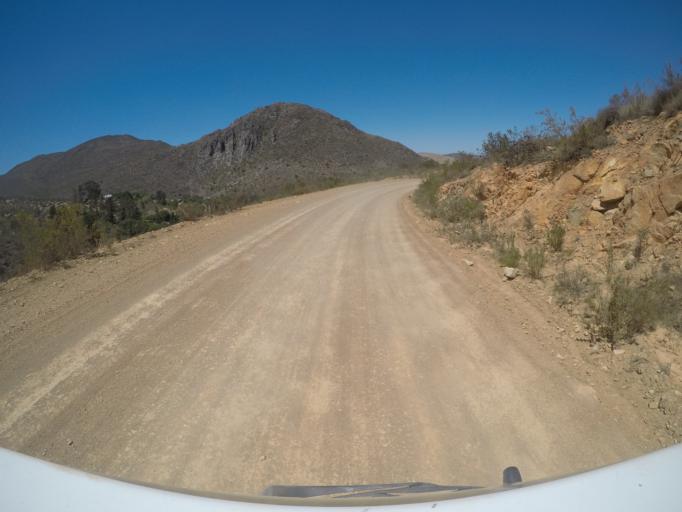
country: ZA
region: Western Cape
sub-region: Overberg District Municipality
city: Grabouw
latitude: -34.1144
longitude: 19.2334
